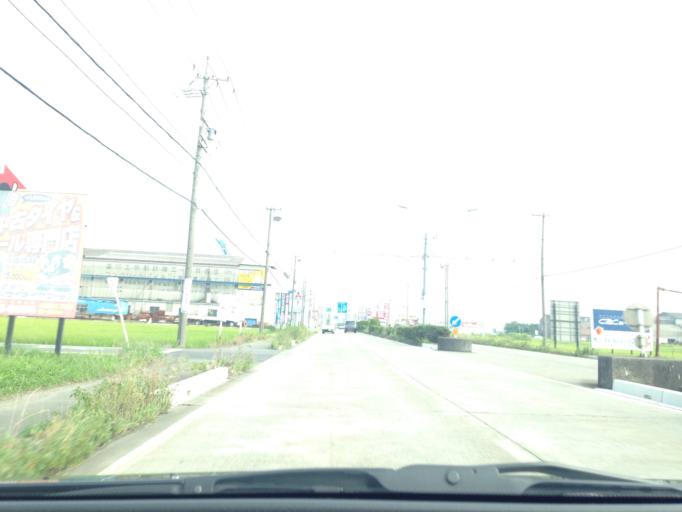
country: JP
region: Aichi
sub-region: Aisai-shi
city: Aisai
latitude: 35.1809
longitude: 136.7750
